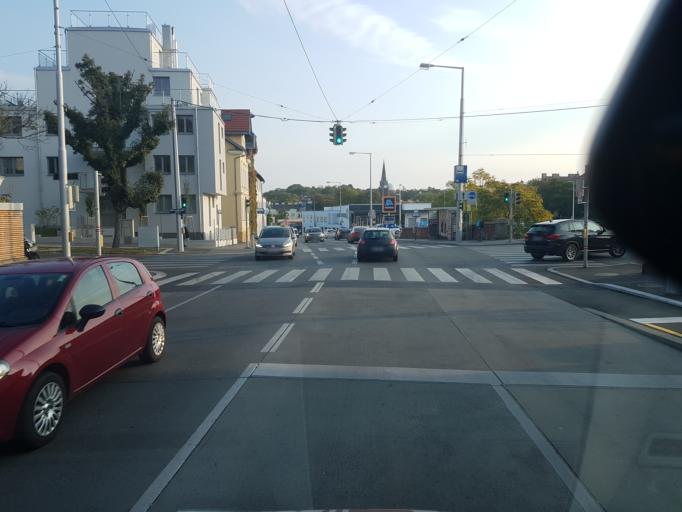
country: AT
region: Vienna
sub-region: Wien Stadt
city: Vienna
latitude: 48.2275
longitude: 16.3271
